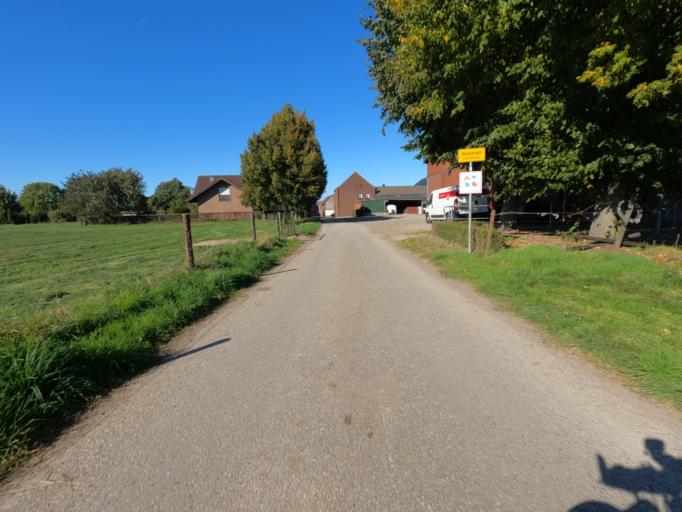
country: DE
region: North Rhine-Westphalia
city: Erkelenz
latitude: 51.0730
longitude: 6.3472
